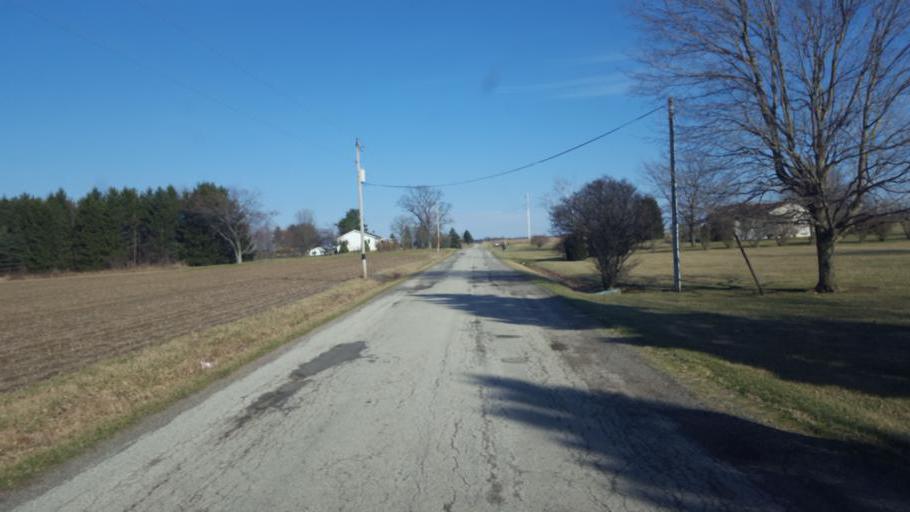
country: US
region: Ohio
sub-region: Crawford County
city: Galion
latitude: 40.6984
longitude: -82.8366
